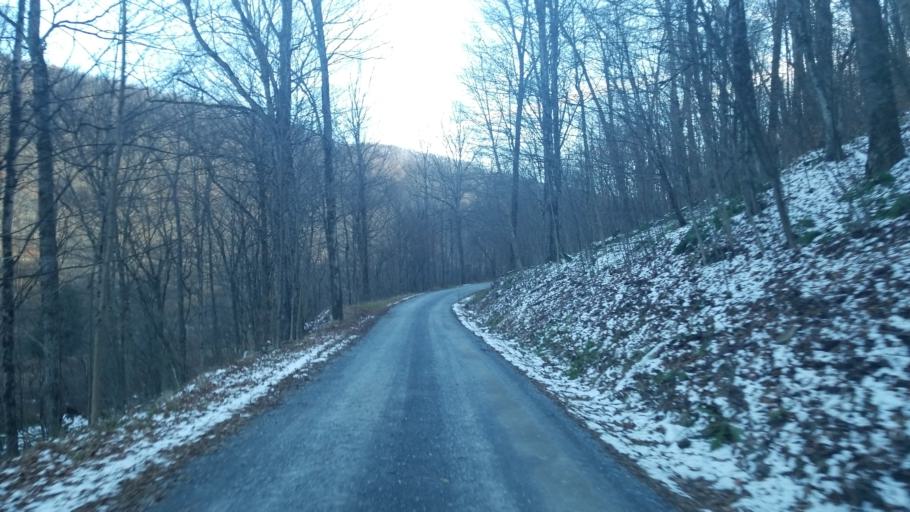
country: US
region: Pennsylvania
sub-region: Potter County
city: Coudersport
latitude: 41.6565
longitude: -78.0869
